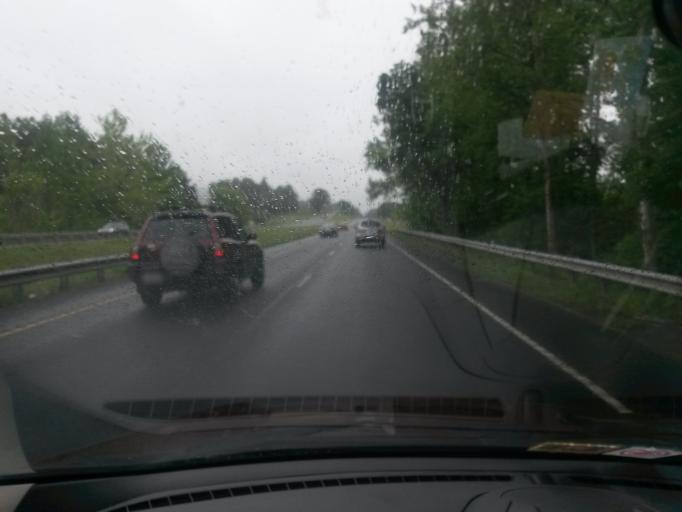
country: US
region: Virginia
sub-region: Albemarle County
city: Hollymead
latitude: 38.1528
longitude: -78.4216
